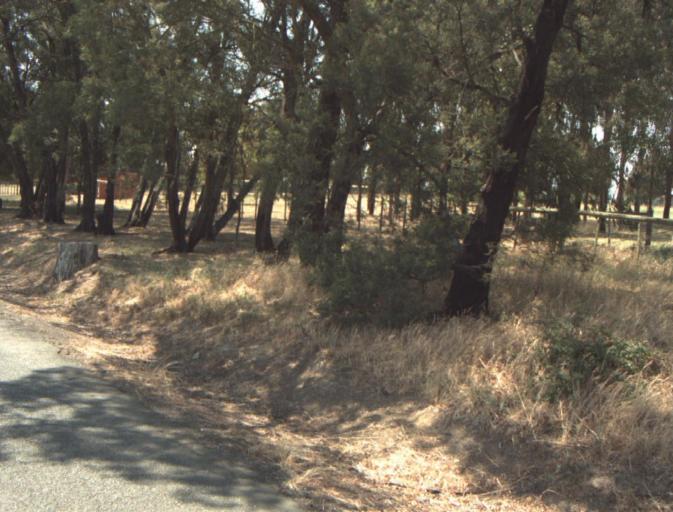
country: AU
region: Tasmania
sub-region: Northern Midlands
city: Perth
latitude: -41.5029
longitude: 147.2055
